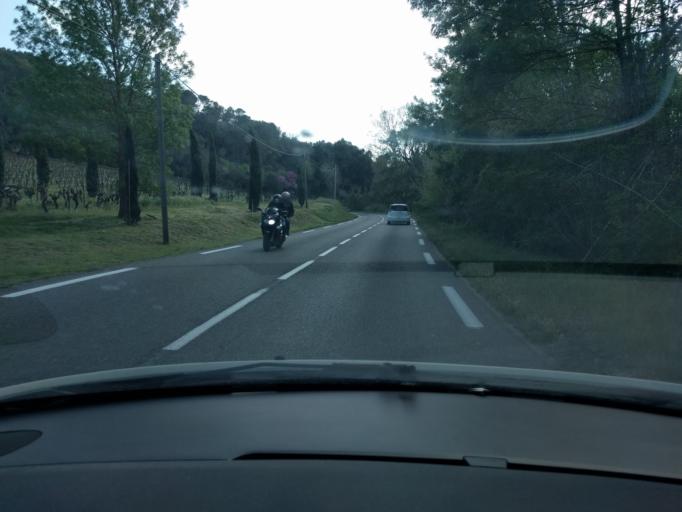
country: FR
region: Provence-Alpes-Cote d'Azur
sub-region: Departement du Var
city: Pierrefeu-du-Var
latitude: 43.2122
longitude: 6.1417
